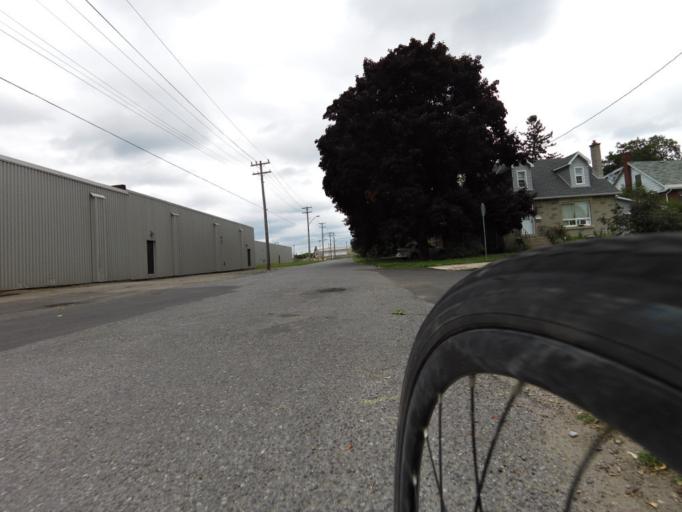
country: CA
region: Ontario
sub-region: Lanark County
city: Smiths Falls
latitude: 44.9026
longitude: -76.0267
